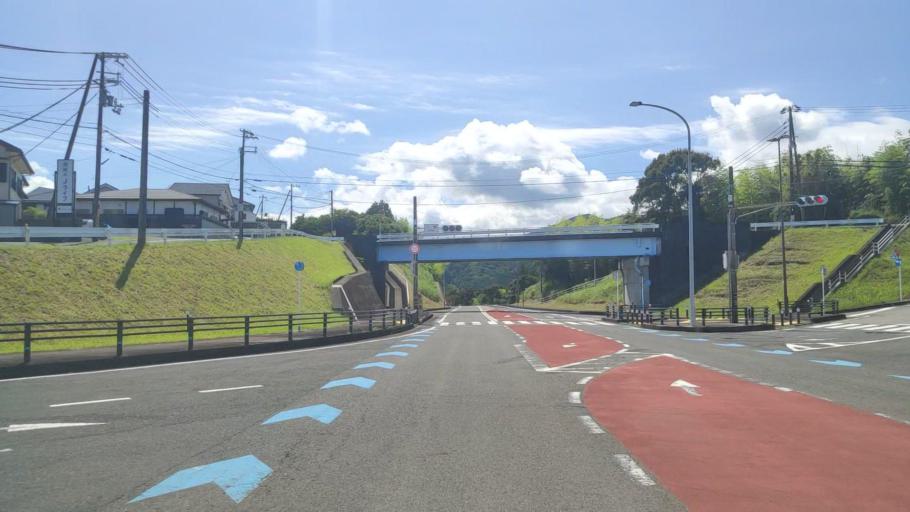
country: JP
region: Wakayama
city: Shingu
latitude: 33.7457
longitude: 136.0146
